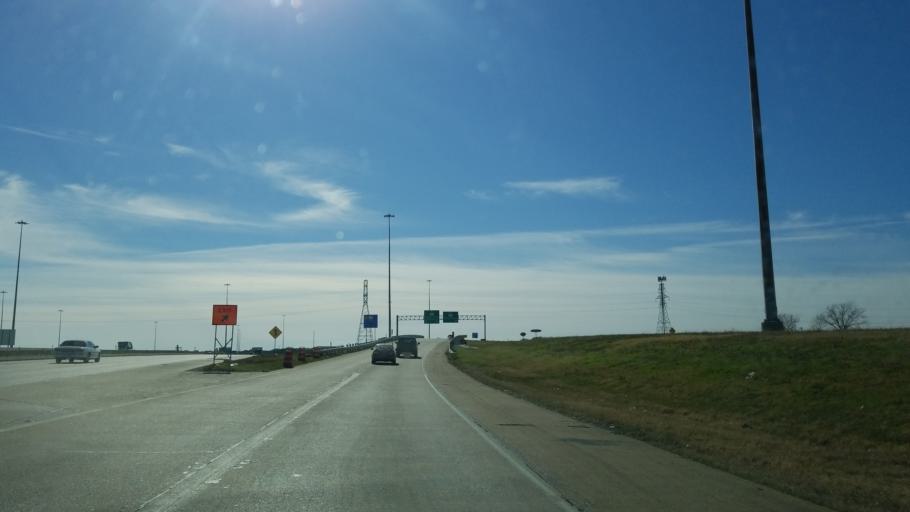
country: US
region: Texas
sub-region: Tarrant County
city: Arlington
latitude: 32.7175
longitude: -97.0630
